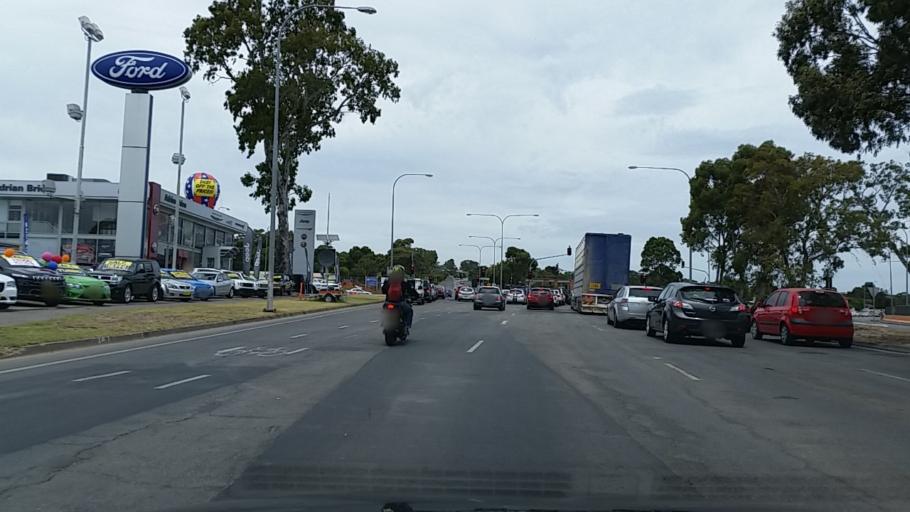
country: AU
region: South Australia
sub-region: Marion
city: Marion
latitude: -35.0101
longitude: 138.5762
